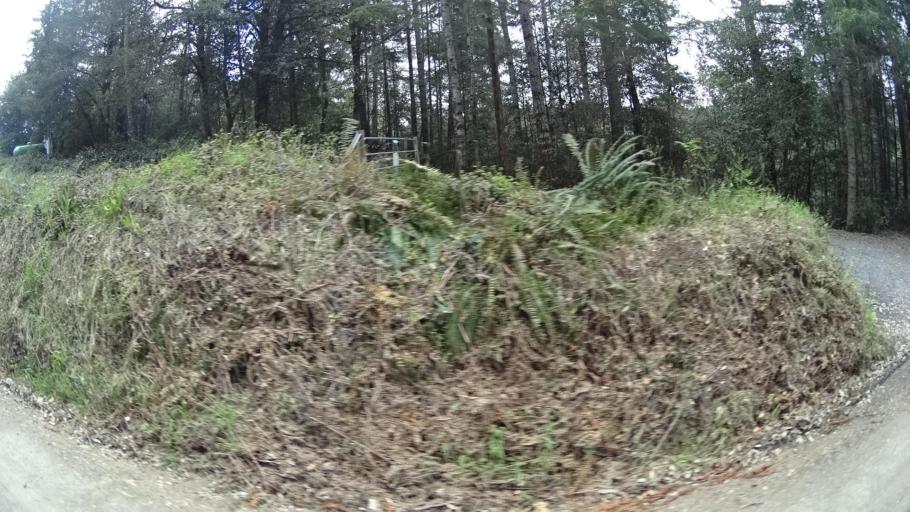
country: US
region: California
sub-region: Humboldt County
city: Blue Lake
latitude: 40.7627
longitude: -123.9561
